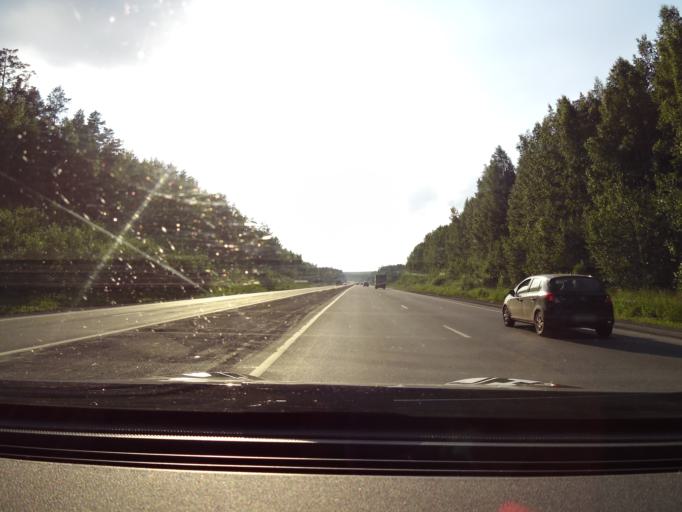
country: RU
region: Sverdlovsk
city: Talitsa
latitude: 56.8419
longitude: 60.1001
